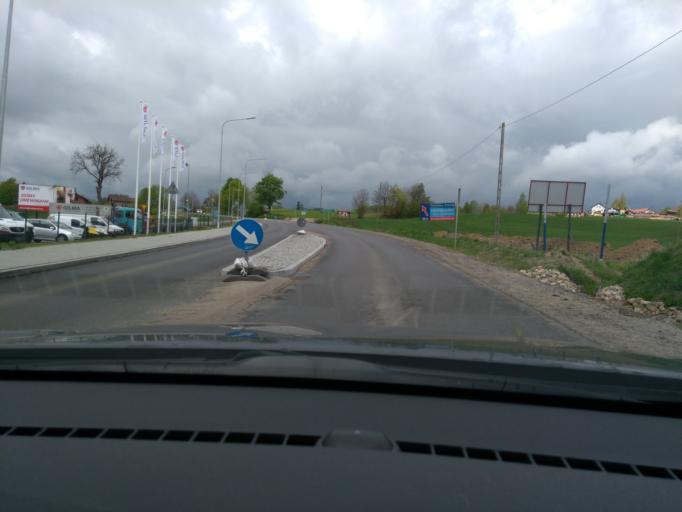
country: PL
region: Pomeranian Voivodeship
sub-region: Powiat kartuski
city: Sierakowice
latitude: 54.3404
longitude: 17.9714
